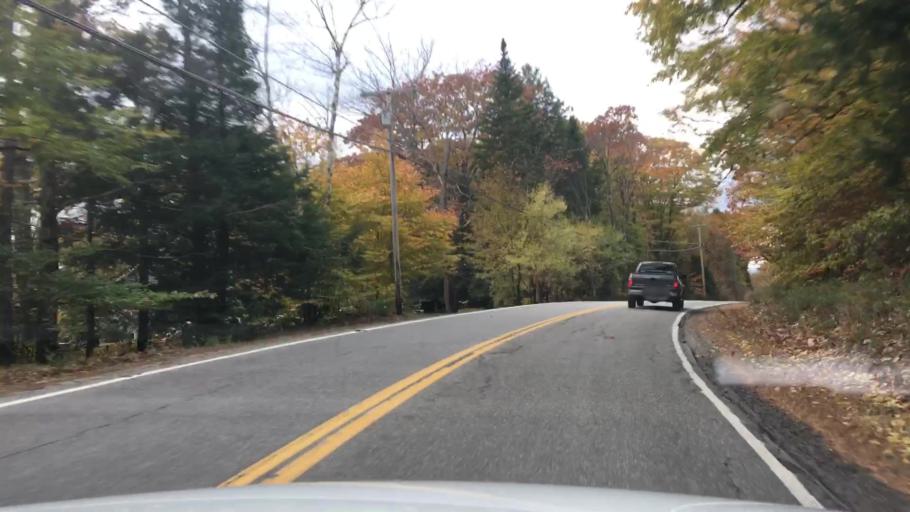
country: US
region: Maine
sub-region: Kennebec County
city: Monmouth
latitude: 44.1346
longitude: -69.9852
